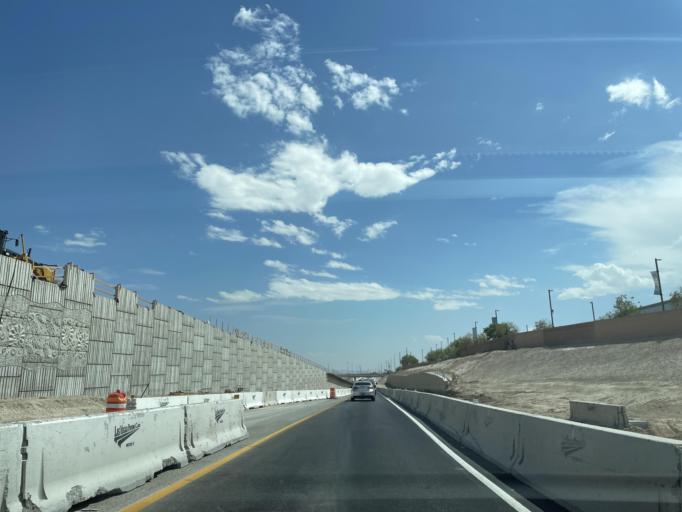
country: US
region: Nevada
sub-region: Clark County
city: Las Vegas
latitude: 36.2763
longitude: -115.2605
